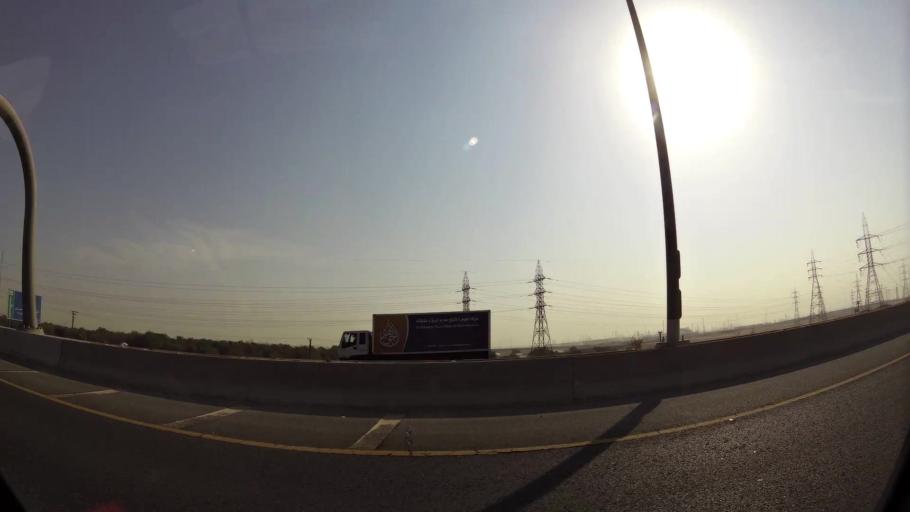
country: KW
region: Al Ahmadi
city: Al Ahmadi
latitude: 29.0732
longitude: 48.0996
